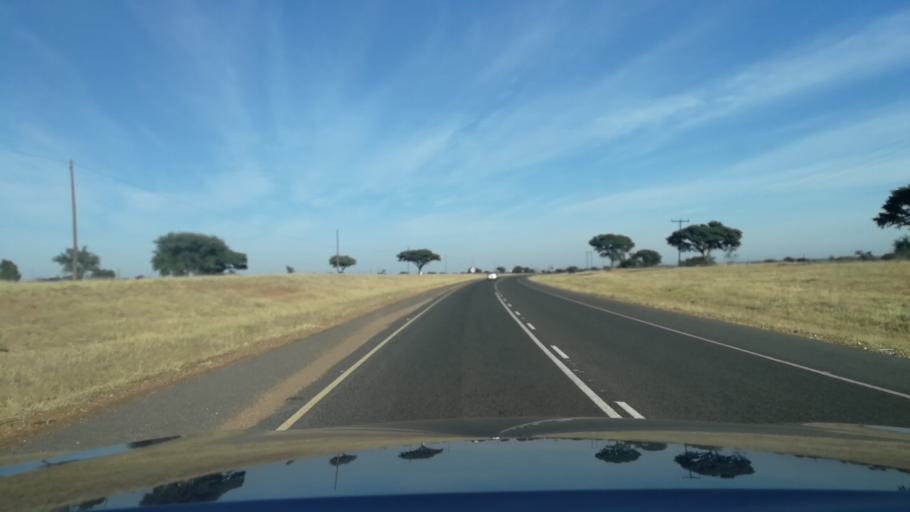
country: BW
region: South East
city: Janeng
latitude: -25.4774
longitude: 25.5146
